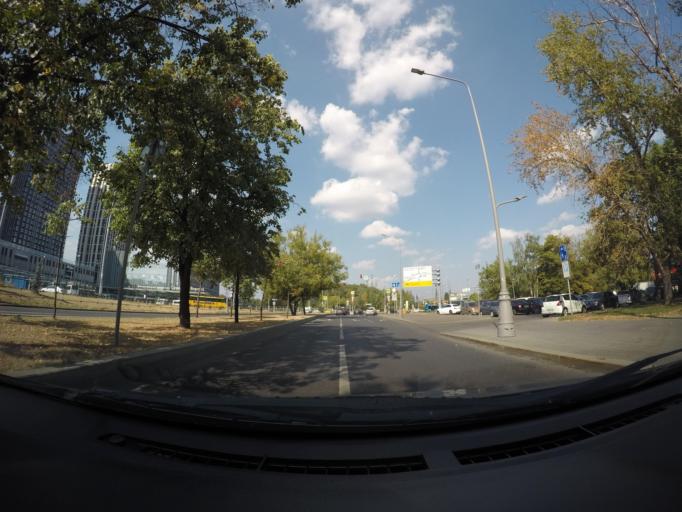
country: RU
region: Moskovskaya
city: Levoberezhnaya
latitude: 55.8780
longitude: 37.4819
